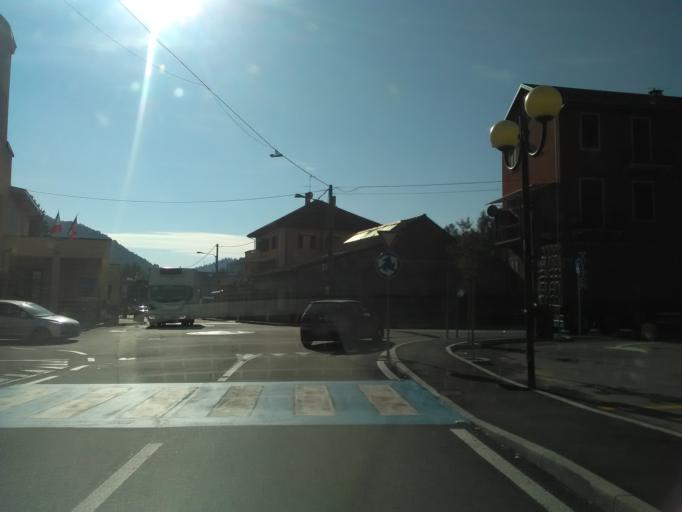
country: IT
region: Piedmont
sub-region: Provincia di Biella
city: Crevacuore
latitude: 45.6858
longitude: 8.2467
